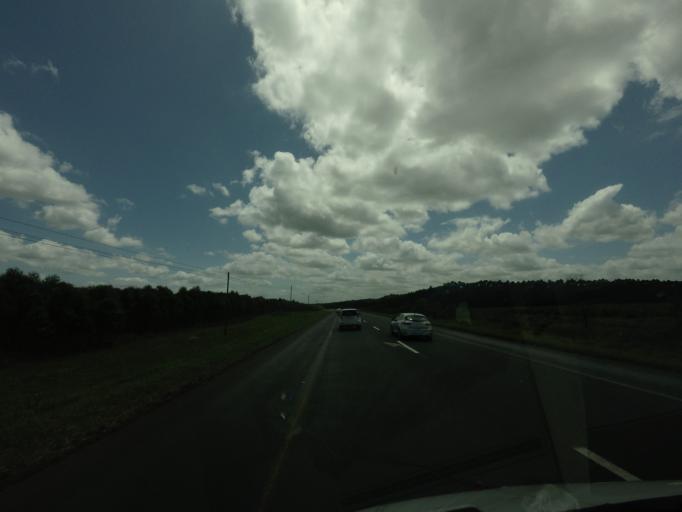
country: ZA
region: KwaZulu-Natal
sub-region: uThungulu District Municipality
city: KwaMbonambi
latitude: -28.5704
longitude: 32.1105
